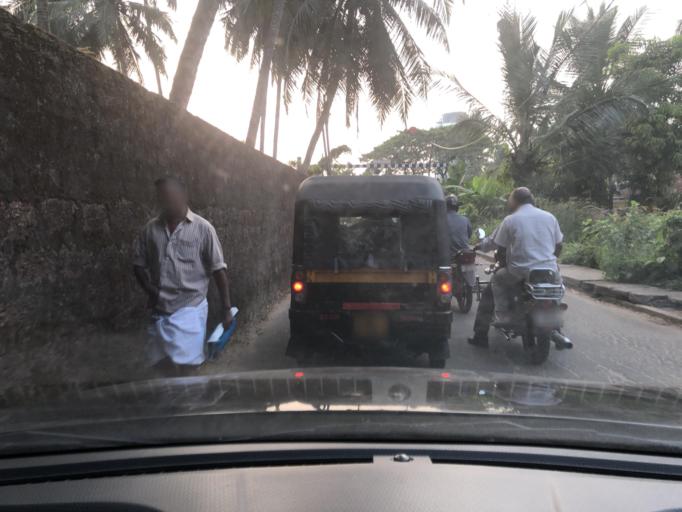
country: IN
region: Kerala
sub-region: Kozhikode
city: Kozhikode
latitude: 11.2919
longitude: 75.7631
